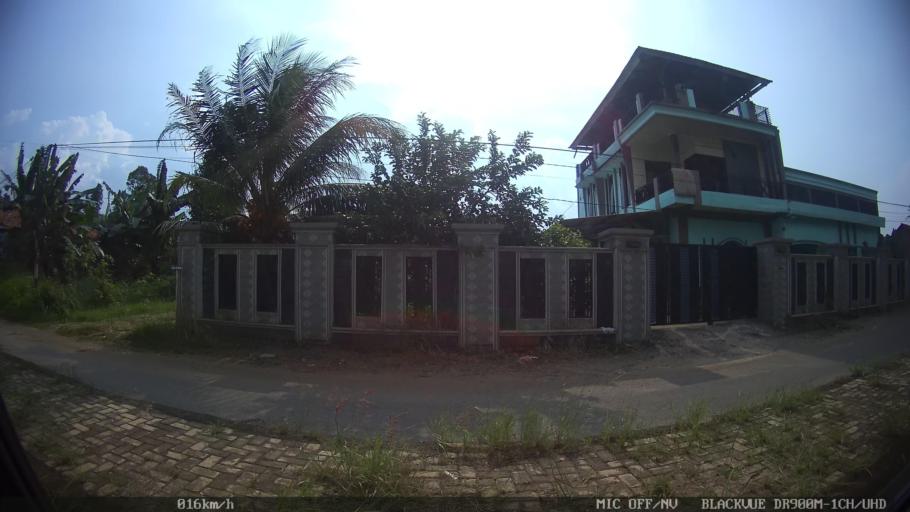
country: ID
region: Lampung
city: Kedaton
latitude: -5.3647
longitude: 105.2139
